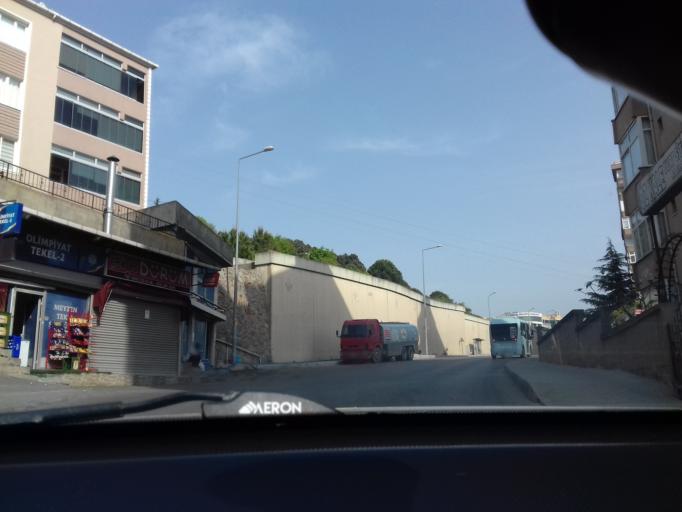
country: TR
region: Istanbul
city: Pendik
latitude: 40.9093
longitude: 29.2359
